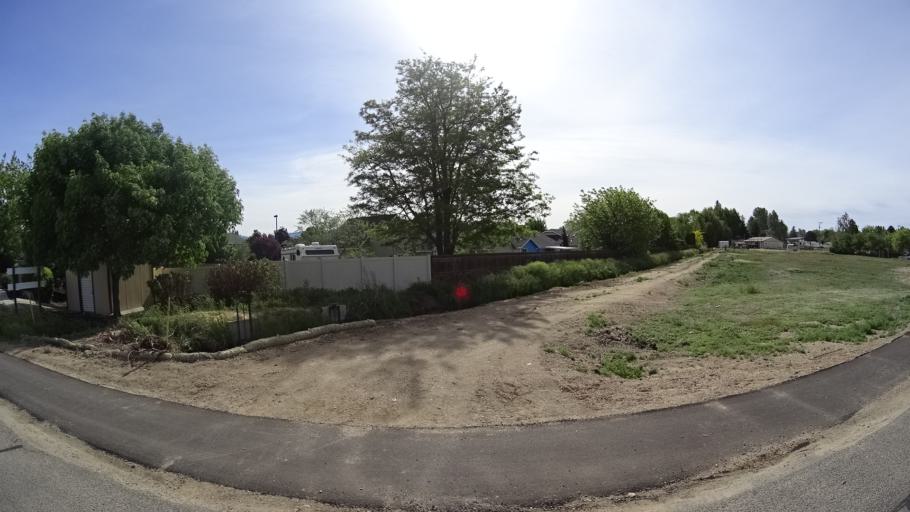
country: US
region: Idaho
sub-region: Ada County
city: Meridian
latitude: 43.5482
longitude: -116.3344
